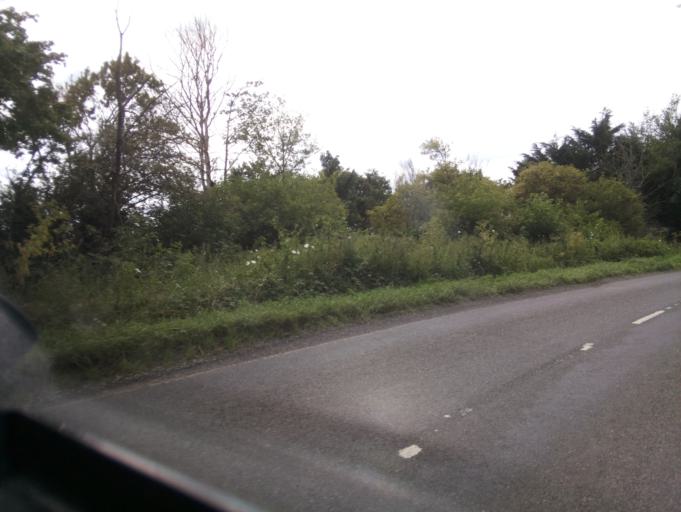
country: GB
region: England
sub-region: Somerset
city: Ilchester
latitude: 51.0505
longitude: -2.6687
